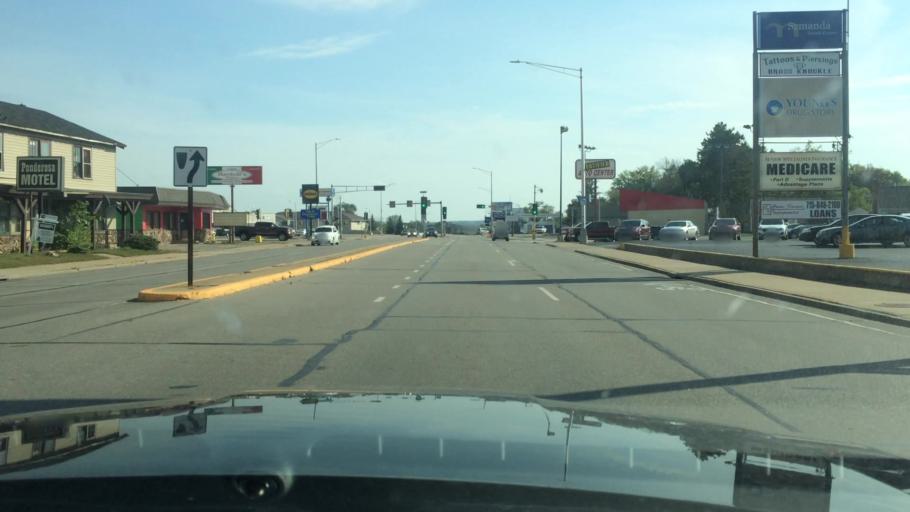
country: US
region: Wisconsin
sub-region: Marathon County
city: Wausau
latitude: 44.9353
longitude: -89.6168
